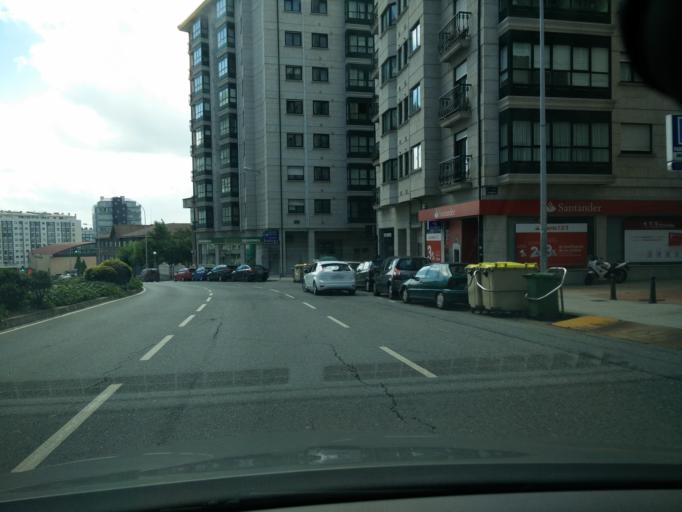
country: ES
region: Galicia
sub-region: Provincia da Coruna
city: A Coruna
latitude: 43.3583
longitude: -8.4195
